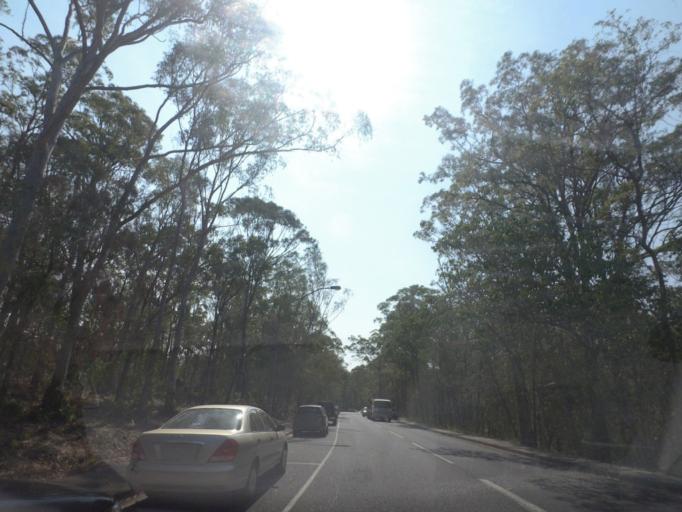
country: AU
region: Queensland
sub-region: Brisbane
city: Nathan
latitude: -27.5508
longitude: 153.0622
